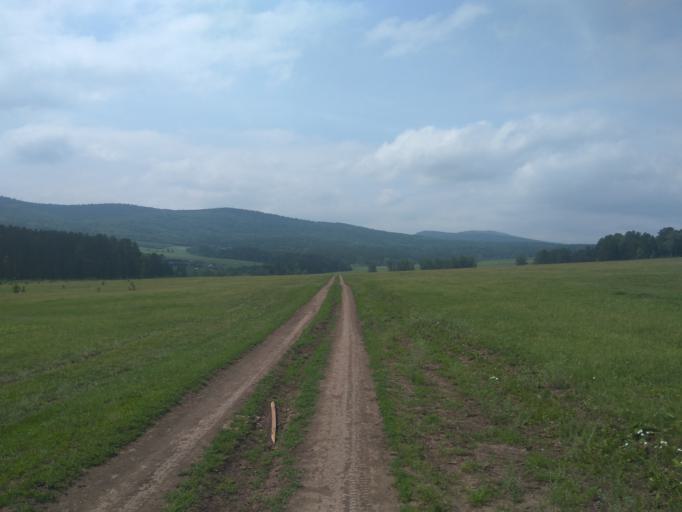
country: RU
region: Krasnoyarskiy
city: Zykovo
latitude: 55.8459
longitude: 93.2075
